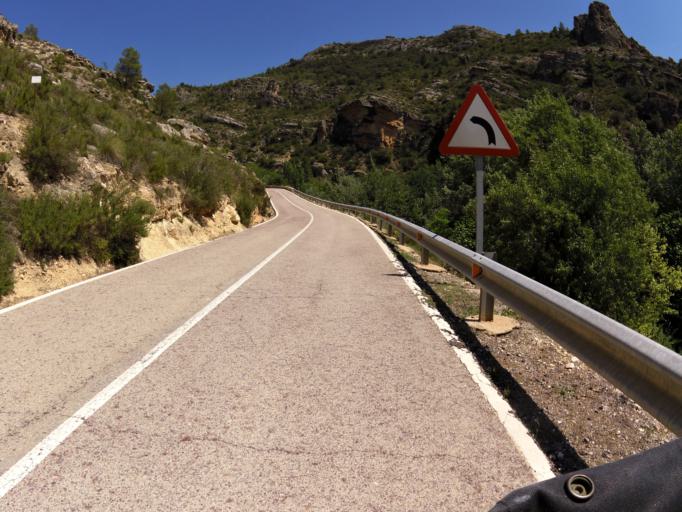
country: ES
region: Valencia
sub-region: Provincia de Valencia
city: Casas Bajas
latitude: 40.0127
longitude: -1.2692
